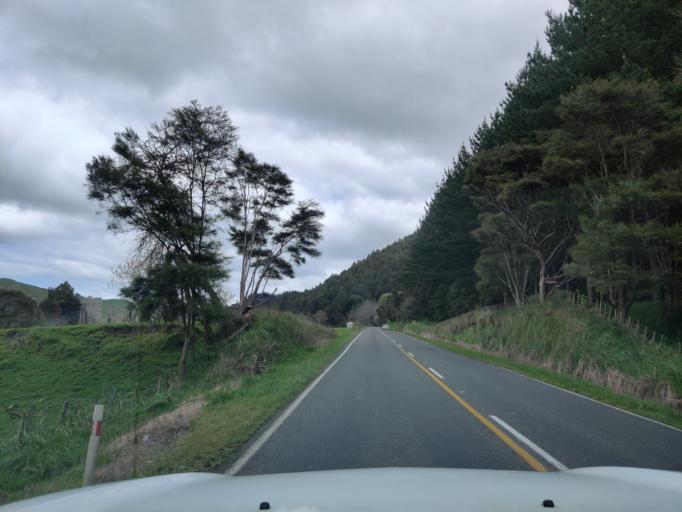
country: NZ
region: Manawatu-Wanganui
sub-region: Wanganui District
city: Wanganui
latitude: -39.8340
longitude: 175.1627
